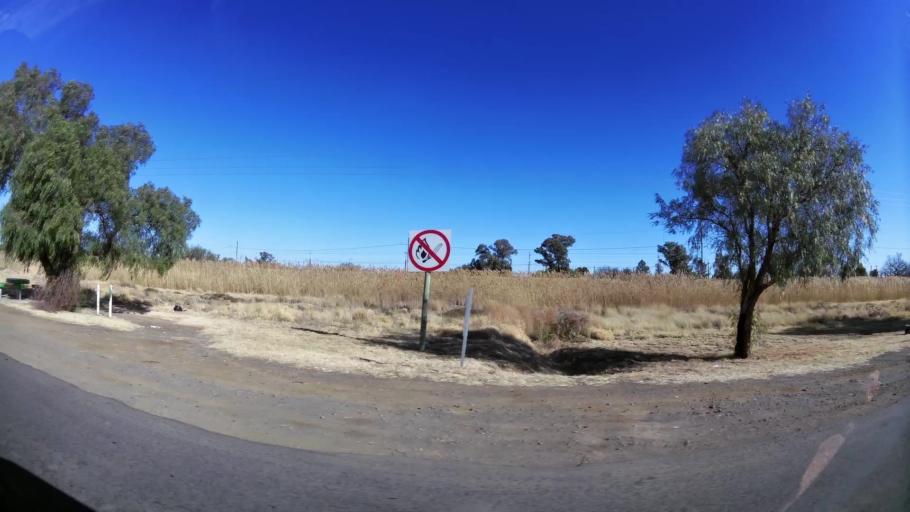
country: ZA
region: Northern Cape
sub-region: Frances Baard District Municipality
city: Kimberley
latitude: -28.7018
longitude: 24.7772
